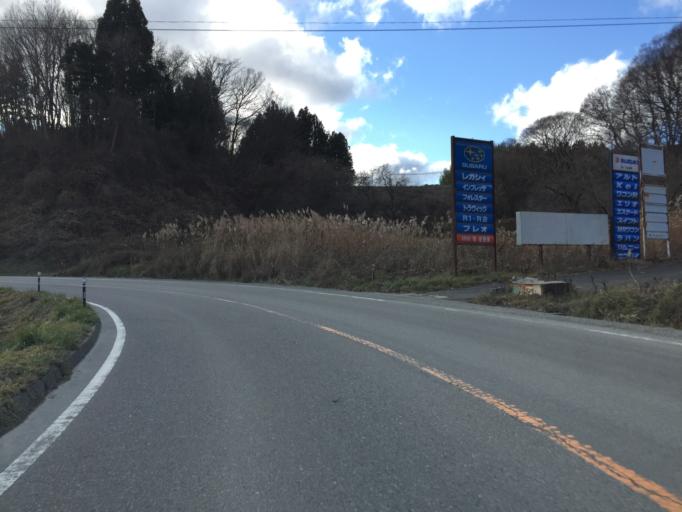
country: JP
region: Fukushima
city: Funehikimachi-funehiki
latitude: 37.5184
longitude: 140.5821
